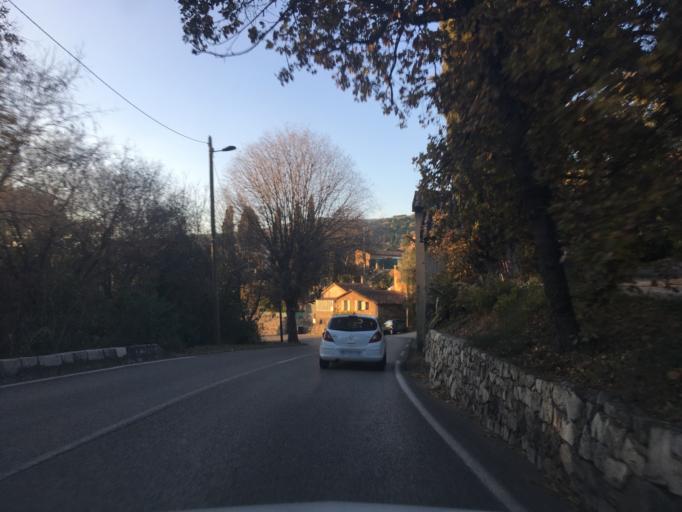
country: FR
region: Provence-Alpes-Cote d'Azur
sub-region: Departement des Alpes-Maritimes
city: Grasse
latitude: 43.6429
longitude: 6.9060
